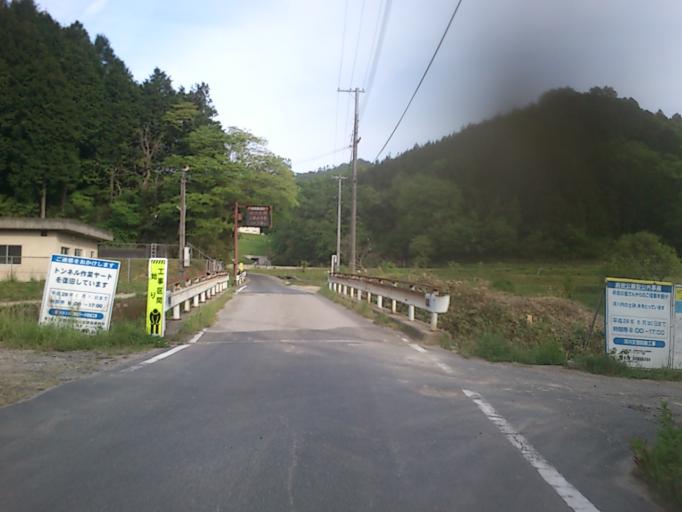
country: JP
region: Kyoto
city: Miyazu
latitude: 35.5681
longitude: 135.1178
